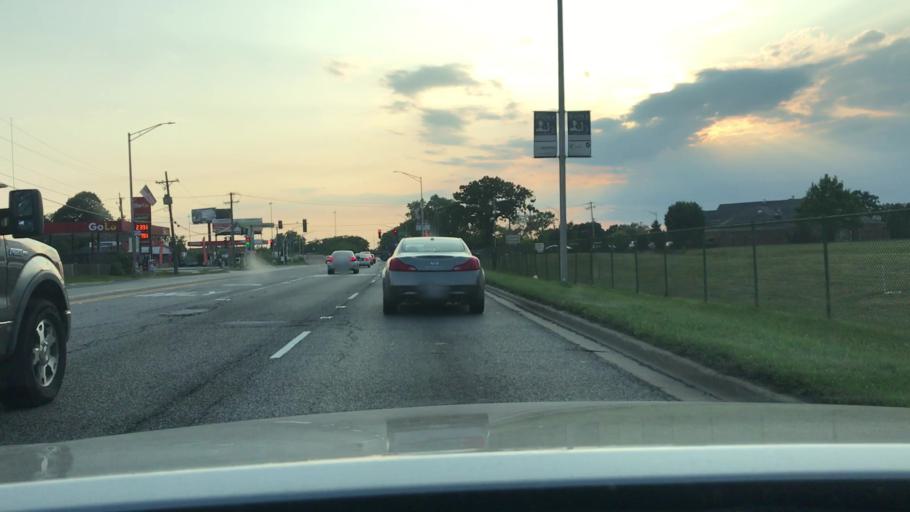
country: US
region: Illinois
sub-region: Cook County
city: Justice
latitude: 41.7474
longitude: -87.8368
